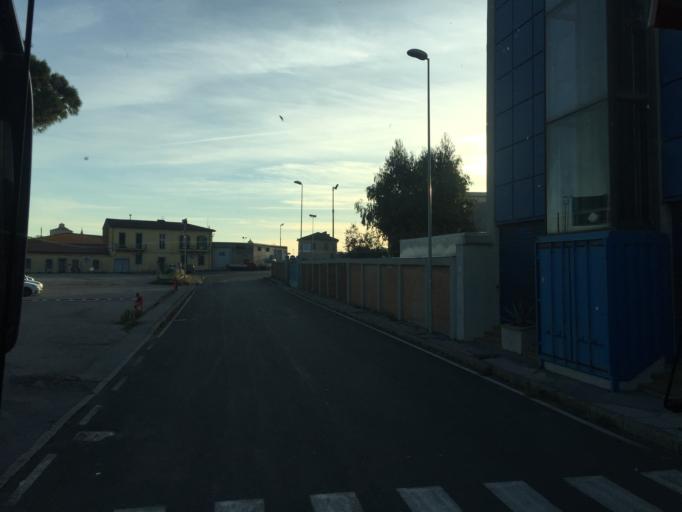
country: IT
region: Tuscany
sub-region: Provincia di Livorno
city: Livorno
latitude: 43.5621
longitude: 10.3090
